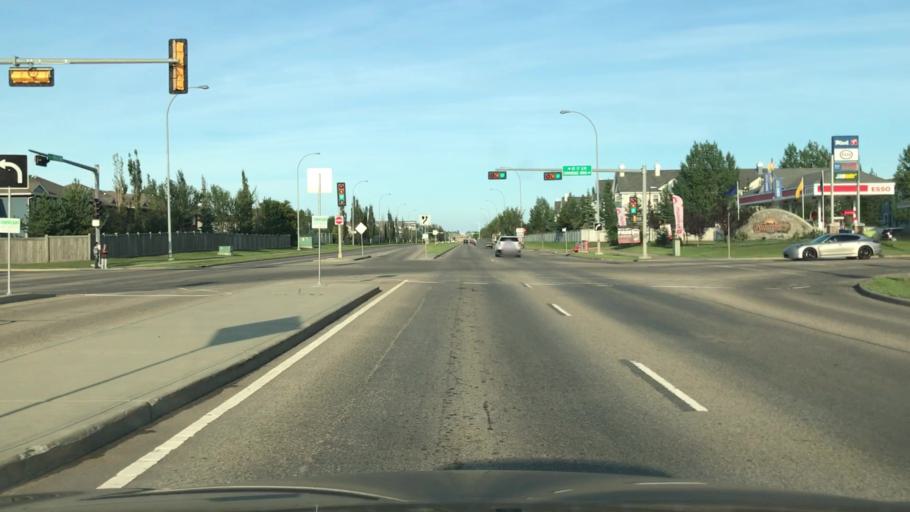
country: CA
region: Alberta
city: Beaumont
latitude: 53.4249
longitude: -113.4635
